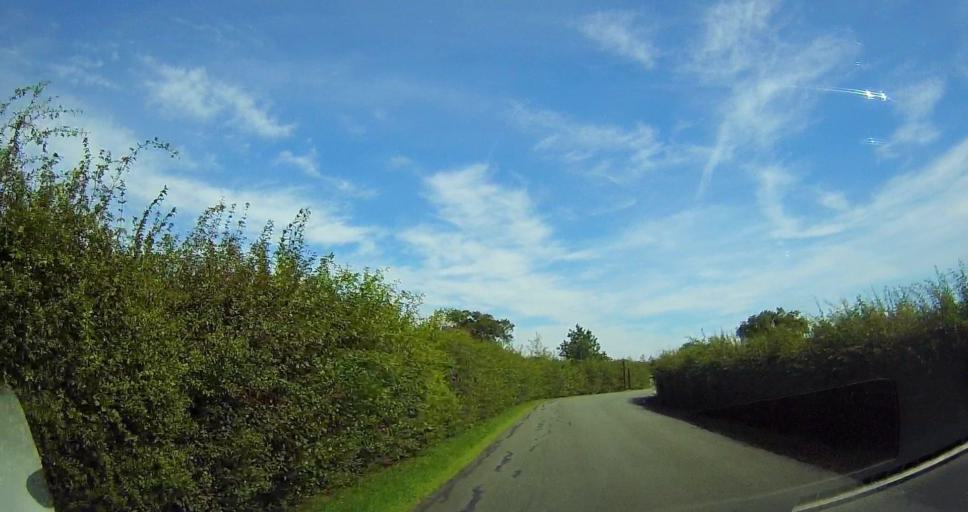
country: GB
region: England
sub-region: Cheshire East
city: Nantwich
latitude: 53.0025
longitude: -2.5254
